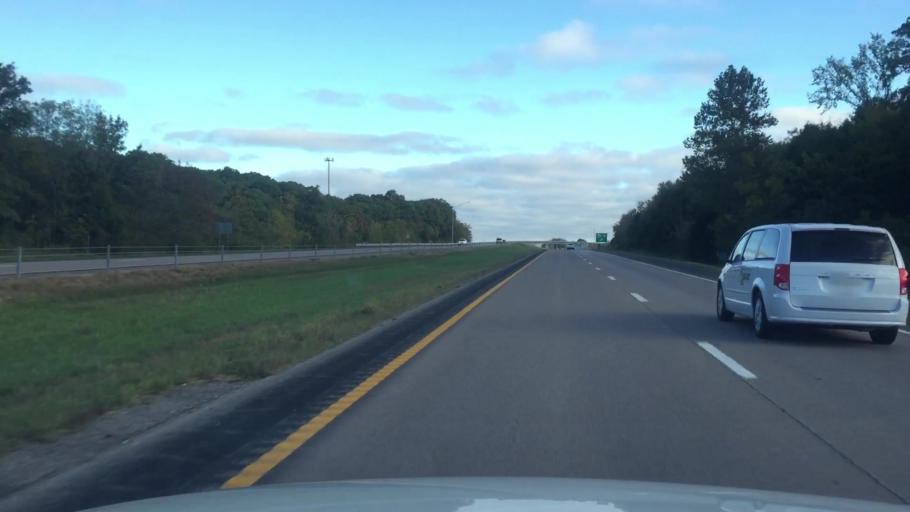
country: US
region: Missouri
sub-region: Boone County
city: Ashland
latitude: 38.8252
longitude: -92.2506
